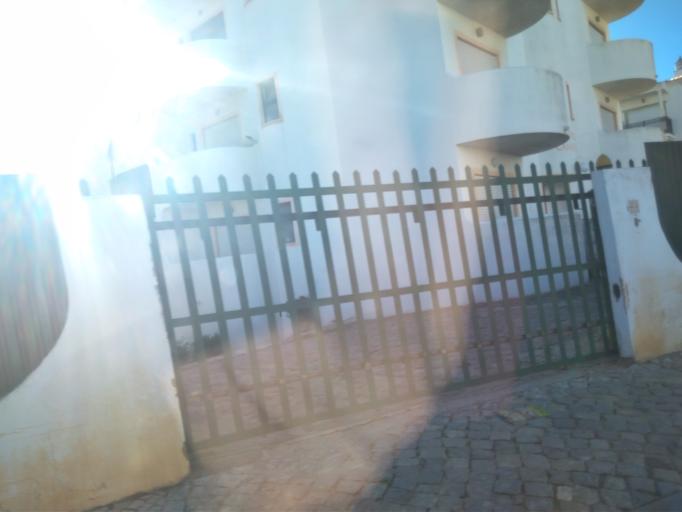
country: PT
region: Faro
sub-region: Albufeira
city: Albufeira
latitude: 37.1035
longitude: -8.2291
